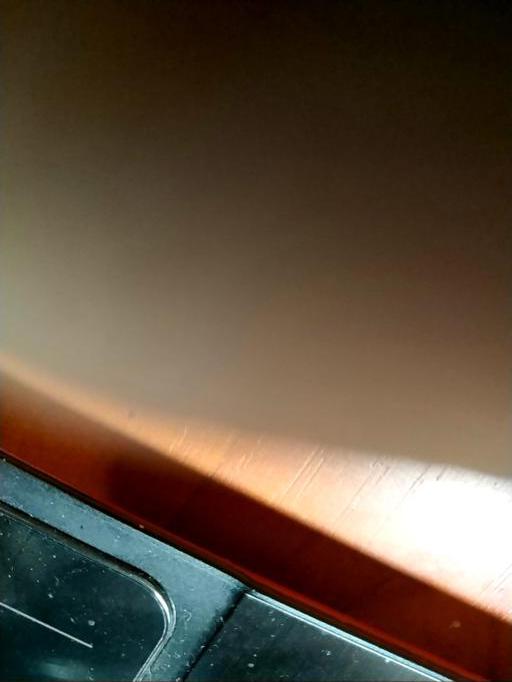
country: RU
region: Rjazan
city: Skopin
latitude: 53.9493
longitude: 39.5108
